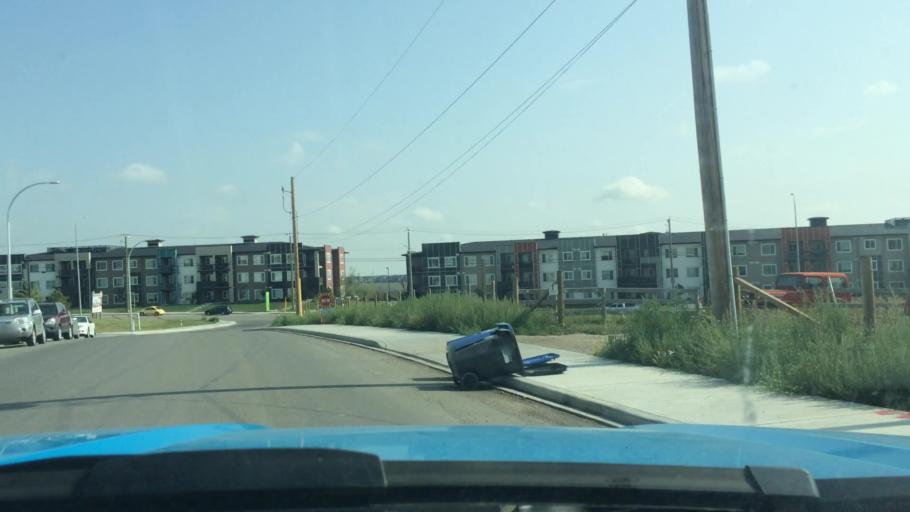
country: CA
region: Alberta
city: Calgary
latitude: 51.1704
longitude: -114.1385
